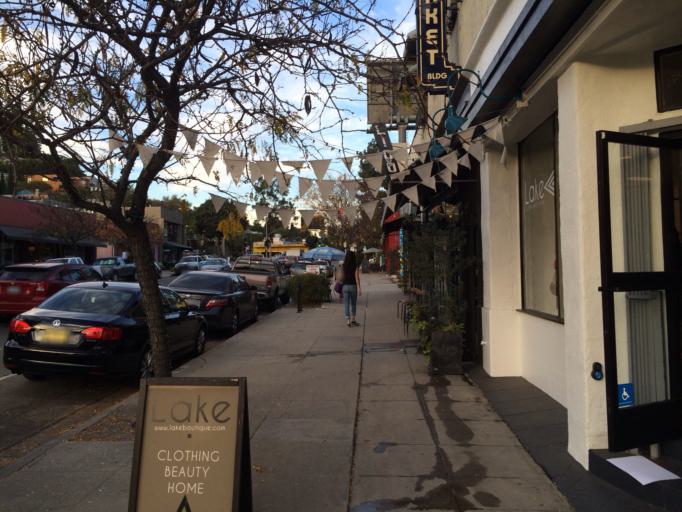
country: US
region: California
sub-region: Los Angeles County
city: Silver Lake
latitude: 34.0884
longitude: -118.2691
